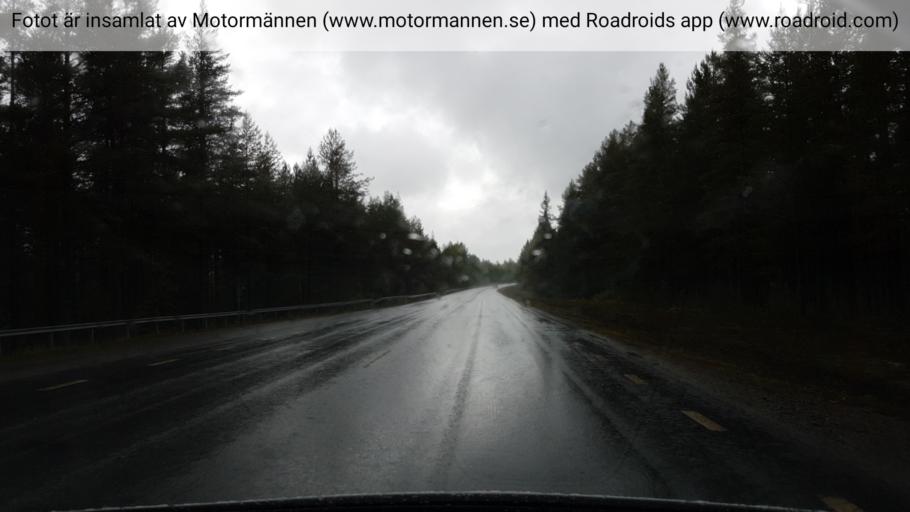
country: SE
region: Vaesterbotten
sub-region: Vindelns Kommun
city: Vindeln
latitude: 64.1429
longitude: 19.8918
